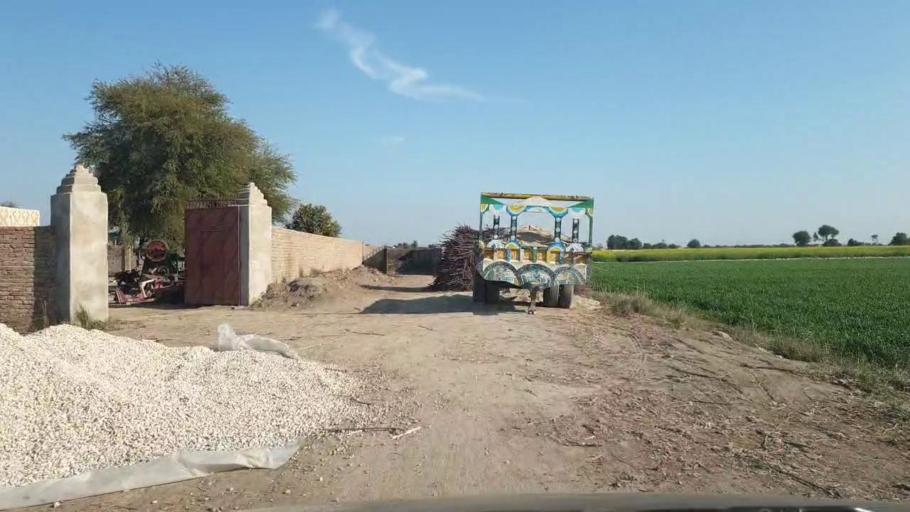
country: PK
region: Sindh
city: Shahpur Chakar
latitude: 26.1753
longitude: 68.6704
